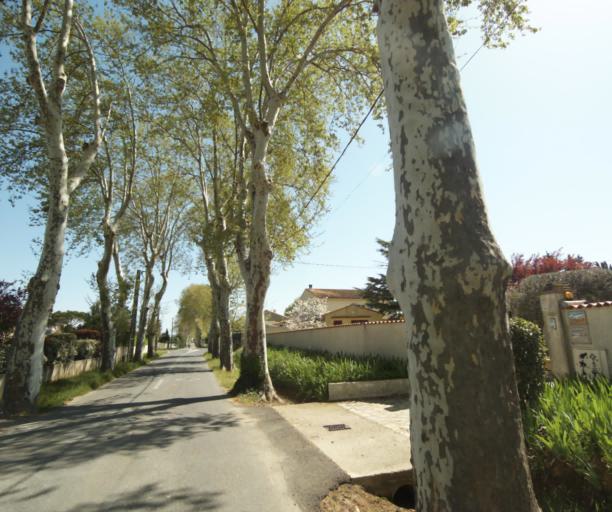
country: FR
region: Languedoc-Roussillon
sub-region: Departement de l'Herault
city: Saint-Drezery
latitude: 43.7277
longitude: 3.9837
